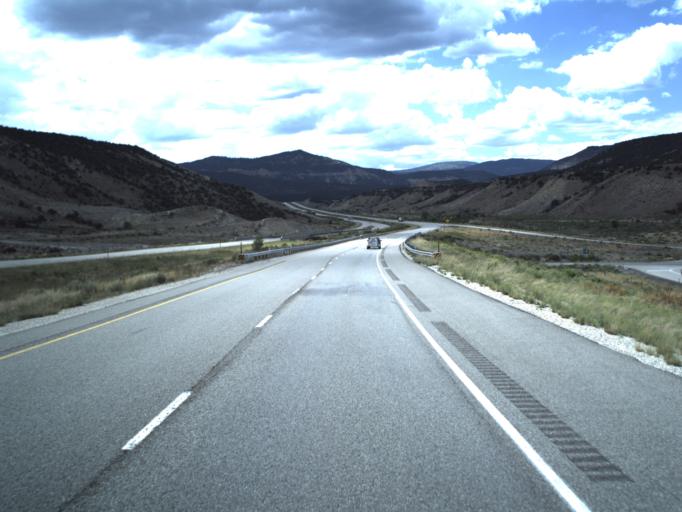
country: US
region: Utah
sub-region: Emery County
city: Ferron
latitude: 38.7667
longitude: -111.3469
